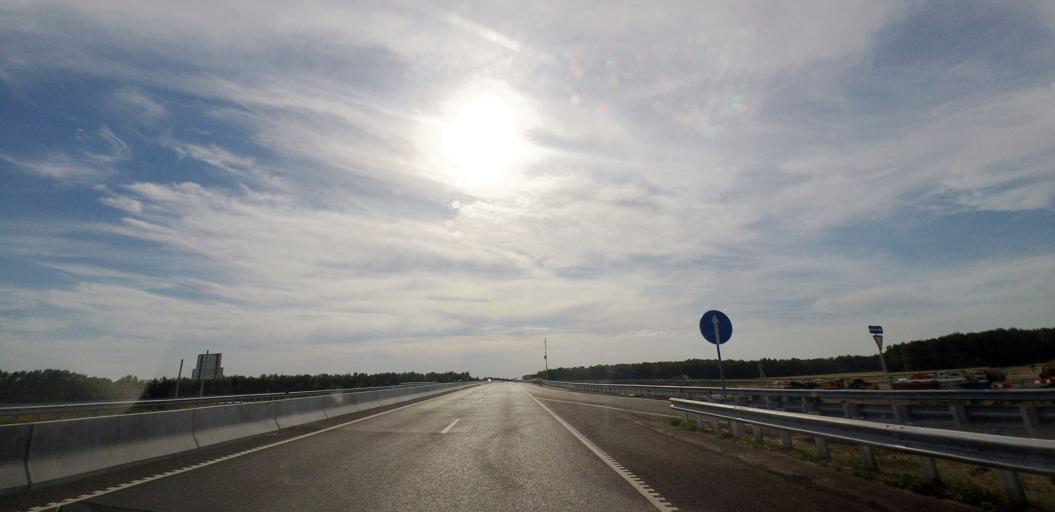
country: BY
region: Grodnenskaya
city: Lida
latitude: 53.8296
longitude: 25.3544
